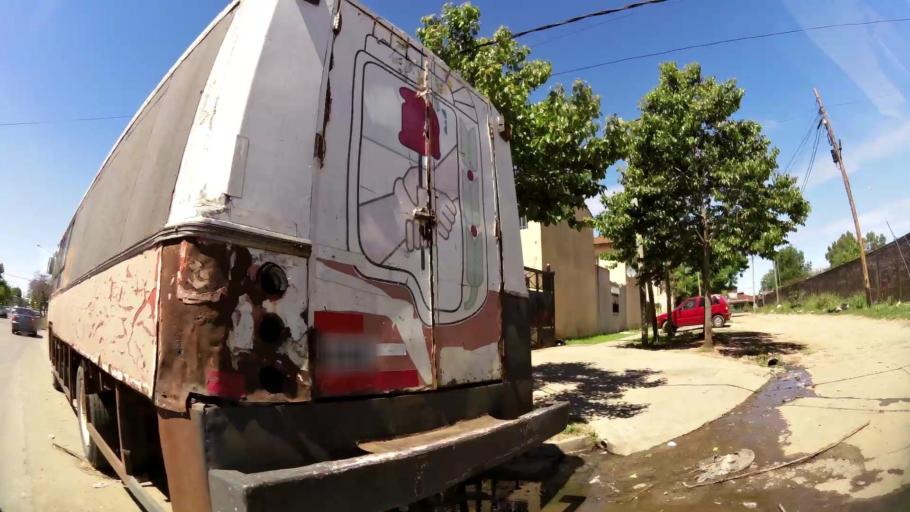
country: AR
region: Buenos Aires
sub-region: Partido de Lanus
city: Lanus
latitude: -34.7382
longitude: -58.3456
